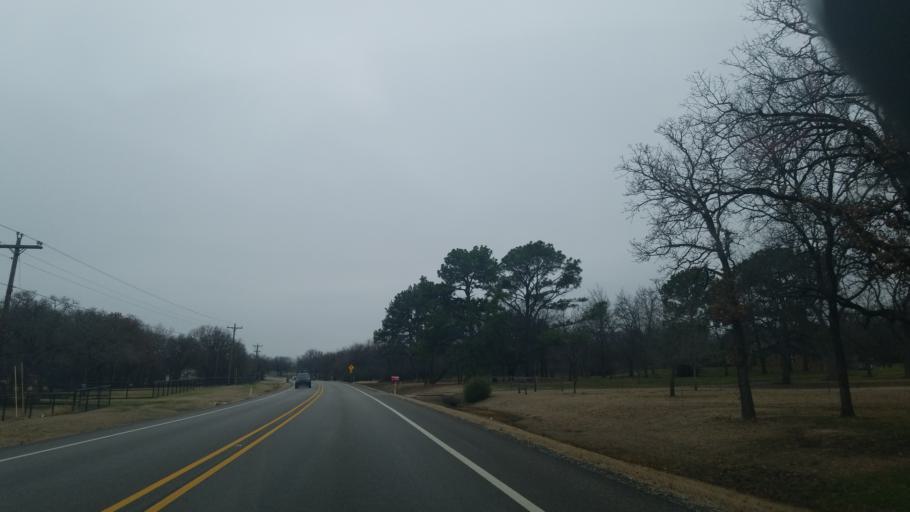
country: US
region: Texas
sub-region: Denton County
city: Argyle
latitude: 33.1413
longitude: -97.1486
